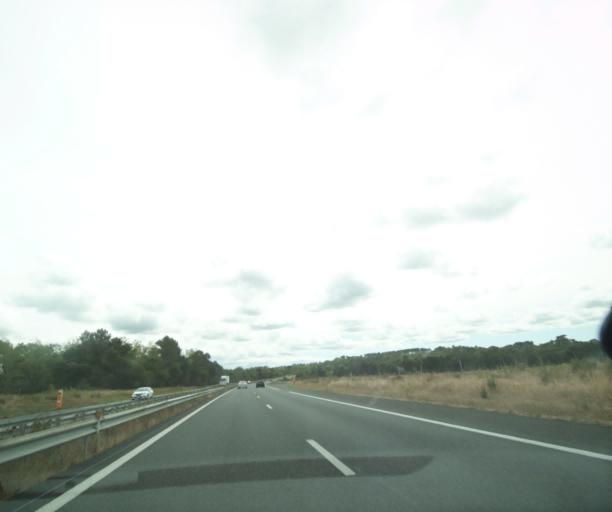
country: FR
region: Aquitaine
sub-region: Departement de la Gironde
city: Reignac
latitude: 45.2250
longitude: -0.5150
